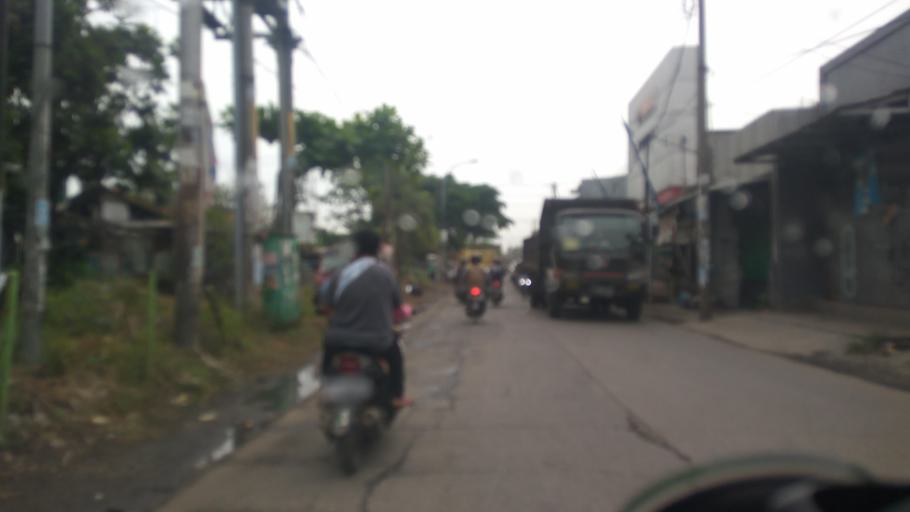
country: ID
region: West Java
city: Bekasi
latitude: -6.2080
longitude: 107.0311
